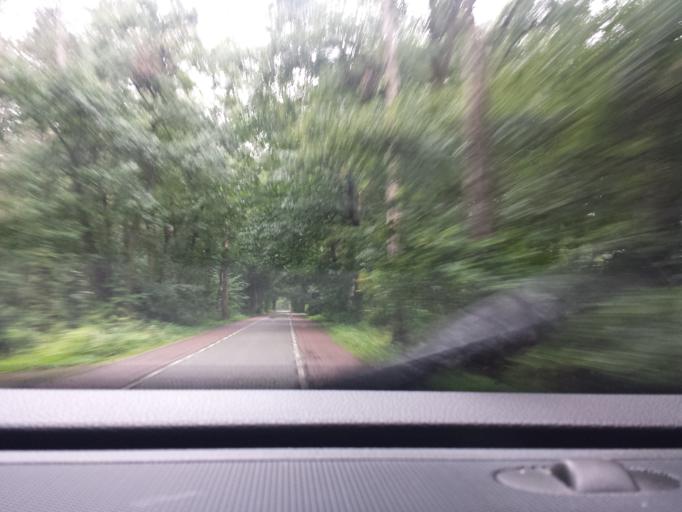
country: NL
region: Gelderland
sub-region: Gemeente Lochem
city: Lochem
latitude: 52.1169
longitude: 6.3617
